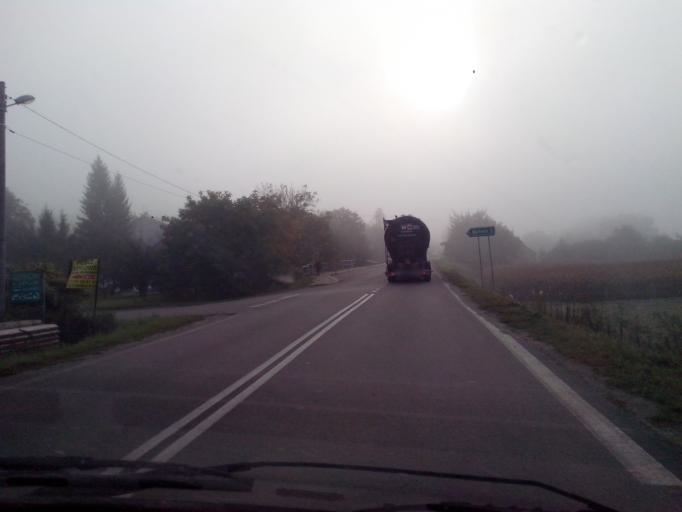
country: PL
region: Subcarpathian Voivodeship
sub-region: Powiat przemyski
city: Krasiczyn
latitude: 49.8082
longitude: 22.7000
